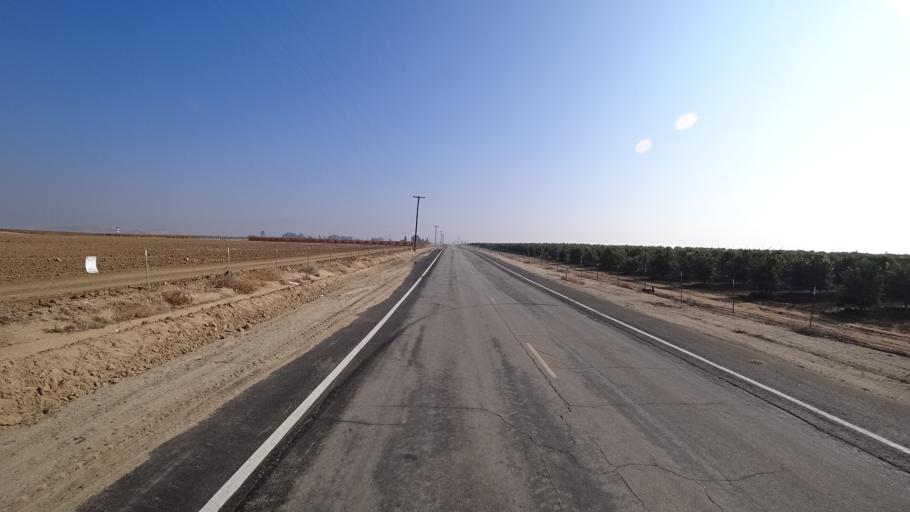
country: US
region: California
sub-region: Kern County
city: Lamont
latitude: 35.3618
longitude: -118.8670
